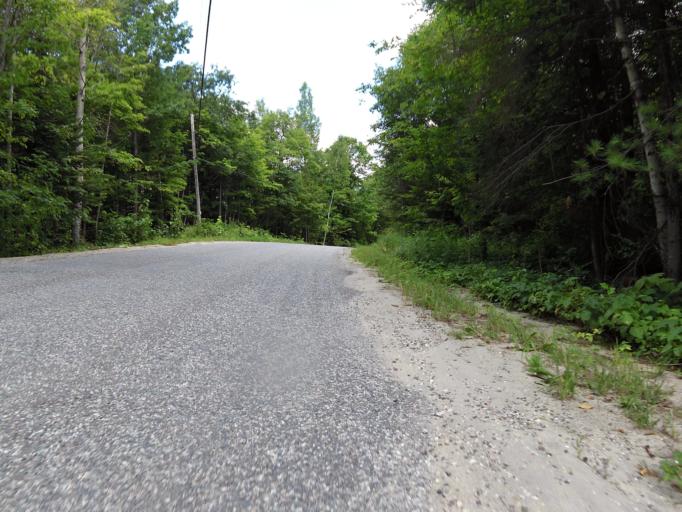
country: CA
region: Quebec
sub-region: Outaouais
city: Wakefield
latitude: 45.8095
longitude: -76.0303
